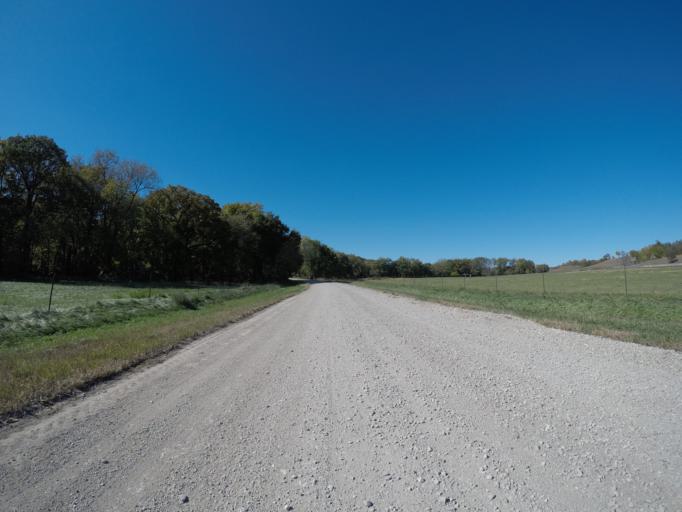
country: US
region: Kansas
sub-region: Wabaunsee County
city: Alma
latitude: 39.0153
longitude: -96.4124
